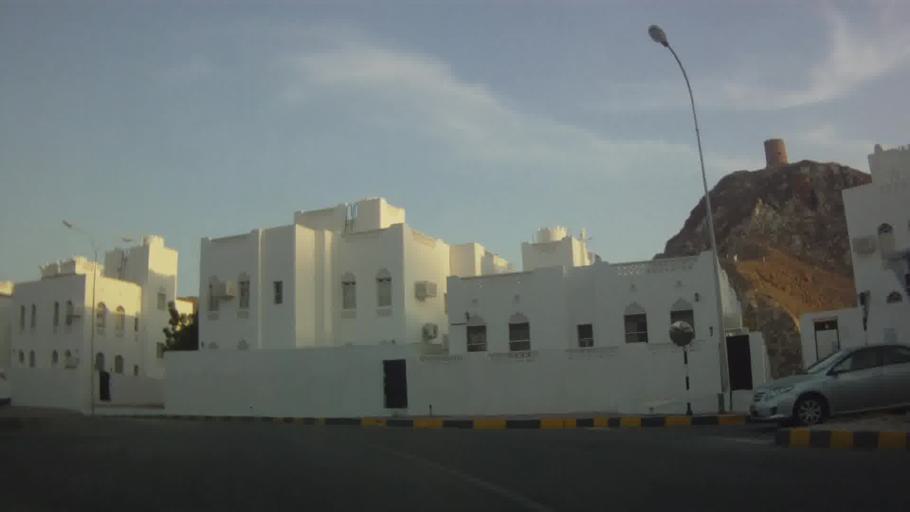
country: OM
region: Muhafazat Masqat
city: Muscat
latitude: 23.6137
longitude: 58.5903
